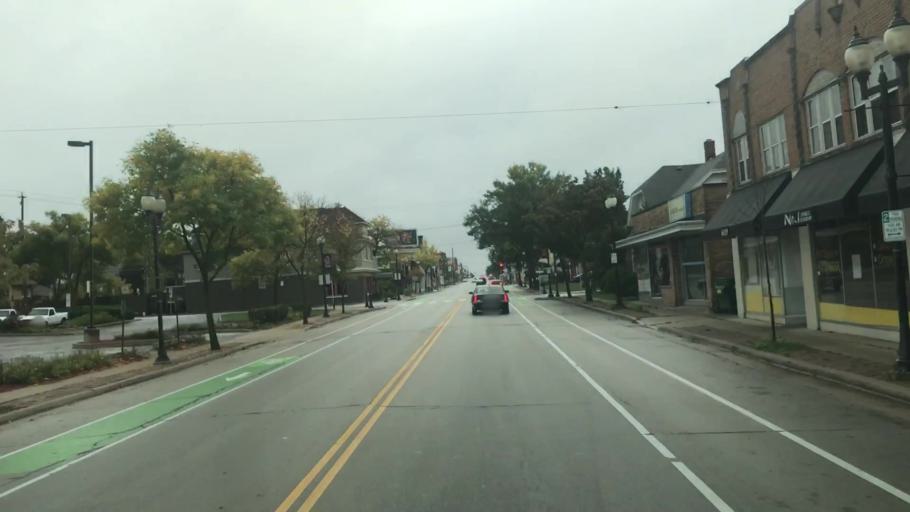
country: US
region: Wisconsin
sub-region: Milwaukee County
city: Wauwatosa
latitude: 43.0607
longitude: -87.9896
